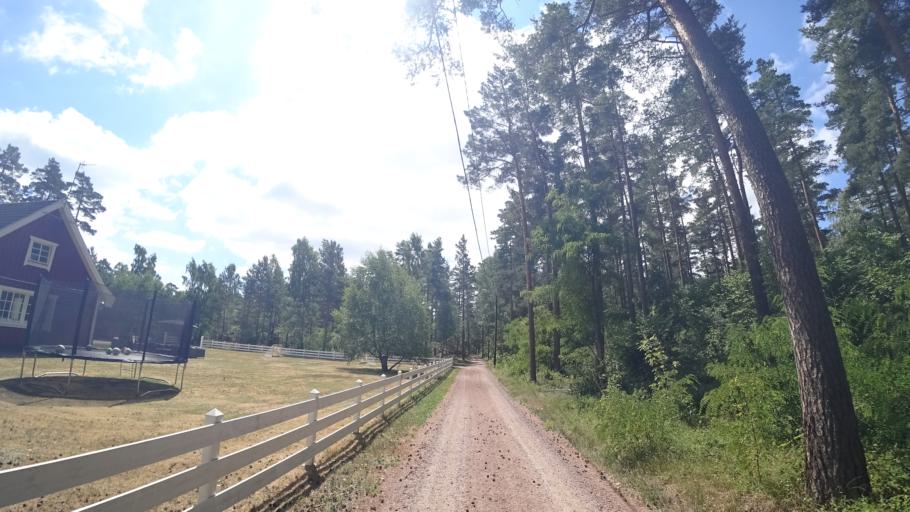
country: SE
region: Skane
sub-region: Kristianstads Kommun
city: Ahus
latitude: 55.9613
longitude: 14.2851
